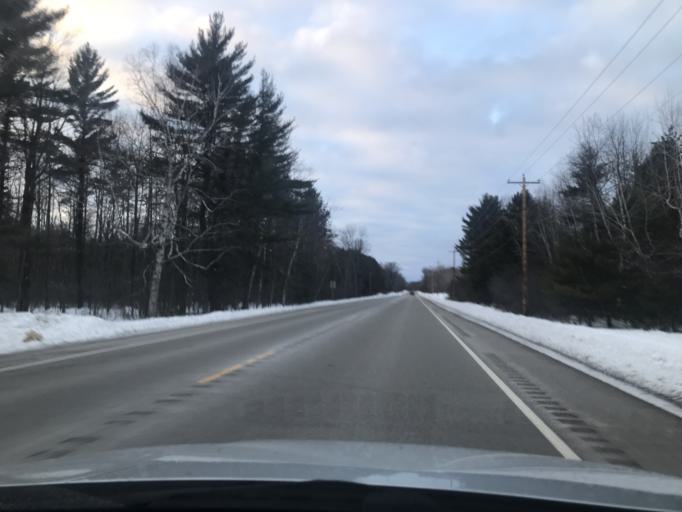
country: US
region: Wisconsin
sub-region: Marinette County
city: Marinette
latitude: 45.1469
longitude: -87.6997
